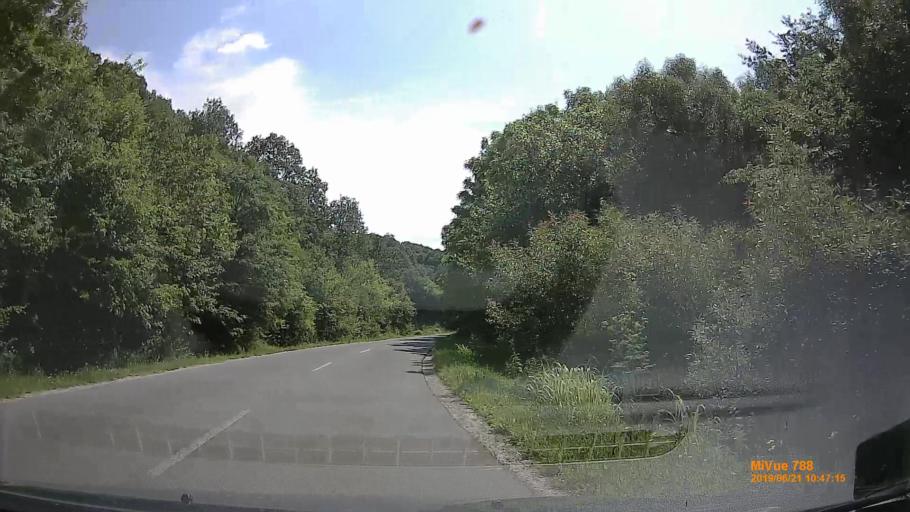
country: HU
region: Baranya
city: Buekkoesd
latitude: 46.1283
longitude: 18.0140
